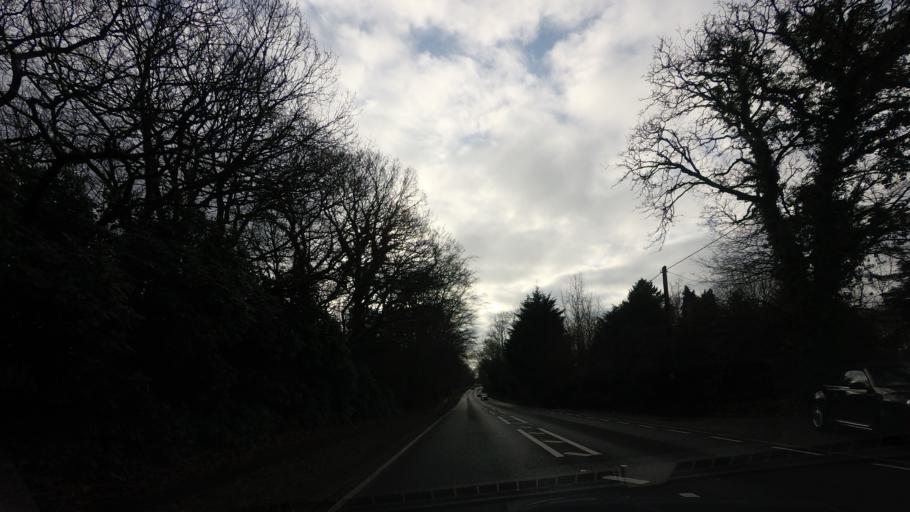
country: GB
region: England
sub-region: Kent
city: Hawkhurst
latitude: 51.0489
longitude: 0.4483
